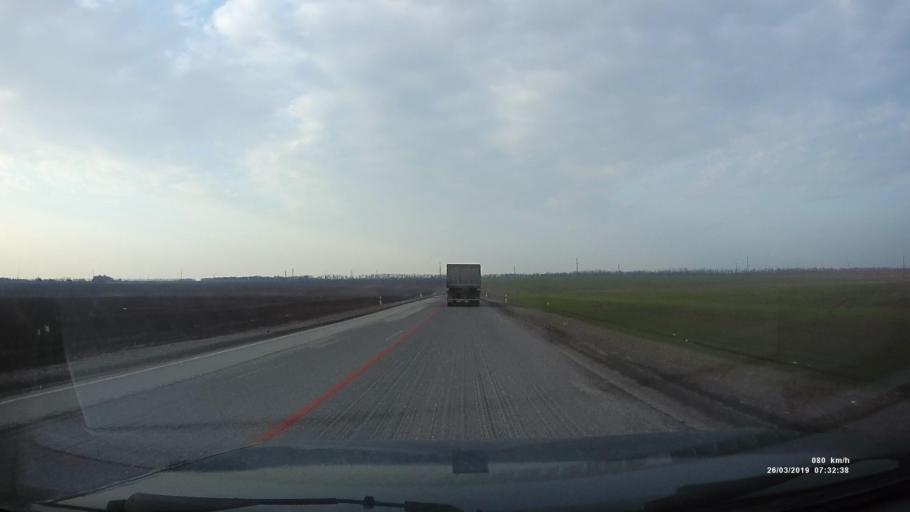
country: RU
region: Rostov
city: Novobessergenovka
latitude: 47.2237
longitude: 38.7763
